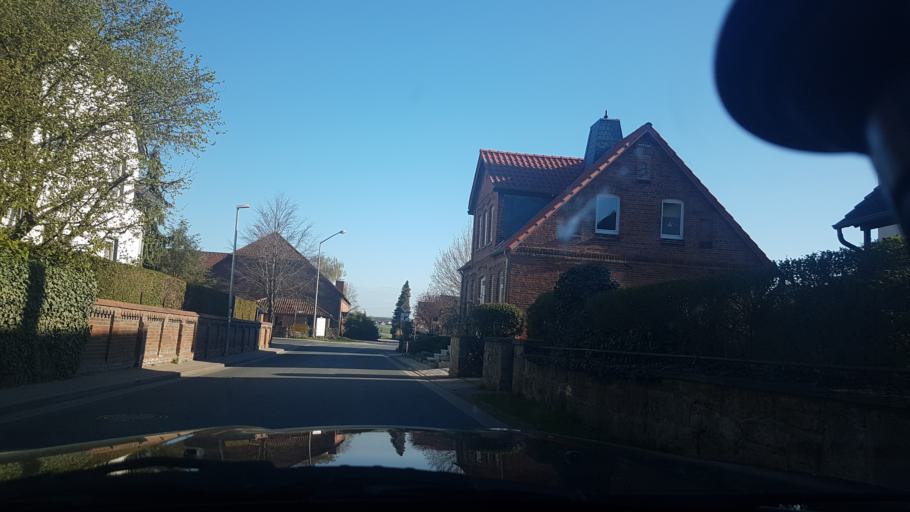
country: DE
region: Lower Saxony
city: Ronnenberg
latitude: 52.2761
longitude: 9.6637
